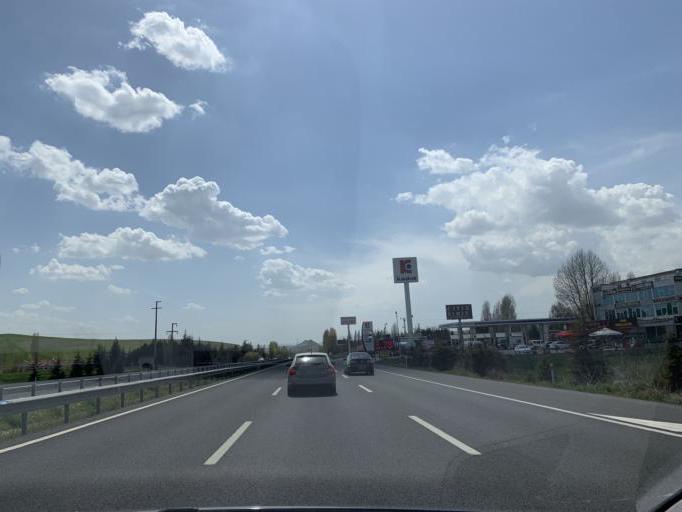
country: TR
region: Ankara
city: Etimesgut
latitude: 39.7975
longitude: 32.5354
